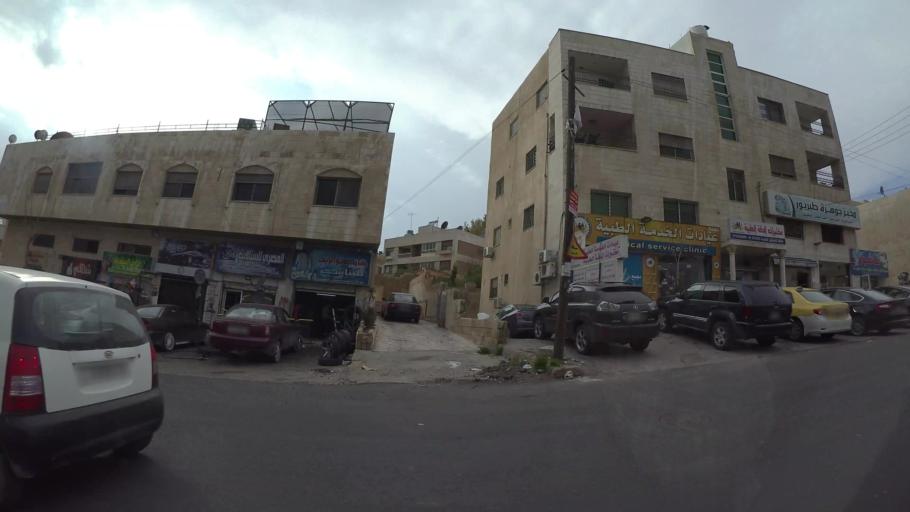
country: JO
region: Amman
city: Amman
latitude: 32.0025
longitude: 35.9492
